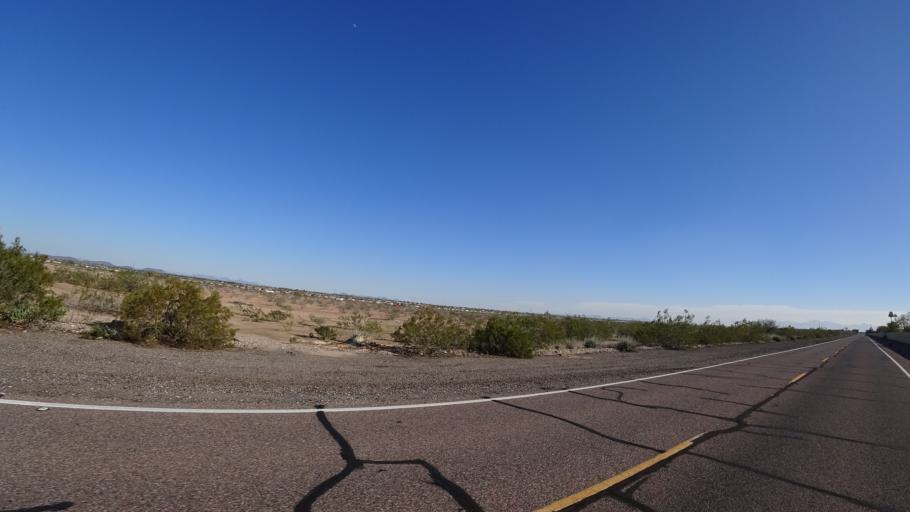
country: US
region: Arizona
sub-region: Maricopa County
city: Sun City West
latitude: 33.6530
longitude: -112.3251
